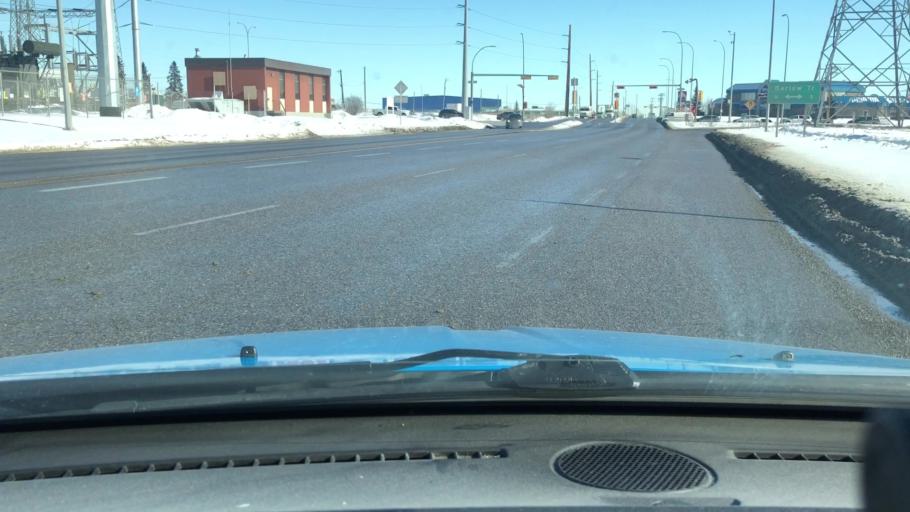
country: CA
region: Alberta
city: Calgary
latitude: 51.0086
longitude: -114.0038
